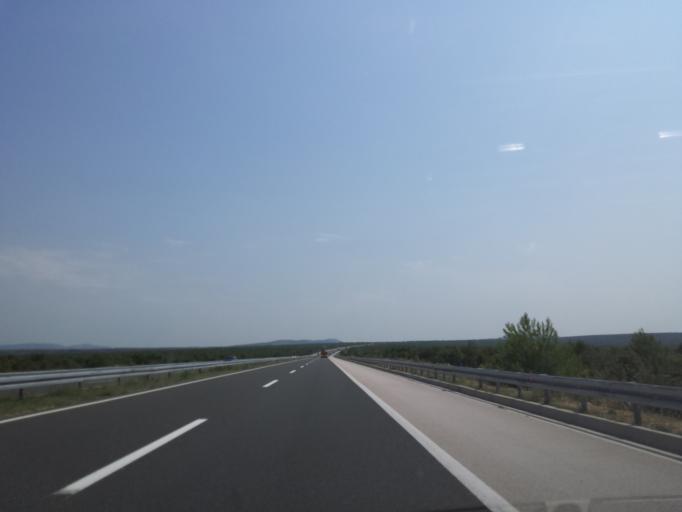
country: HR
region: Zadarska
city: Benkovac
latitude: 43.9965
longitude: 15.6120
